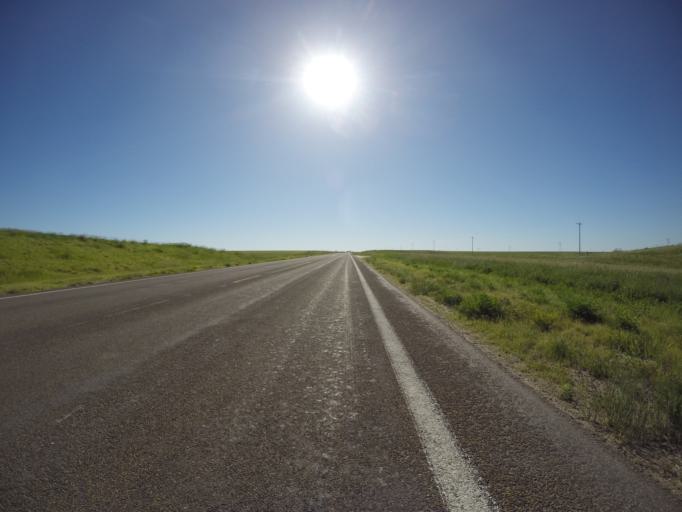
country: US
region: Kansas
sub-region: Norton County
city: Norton
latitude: 39.8281
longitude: -100.0194
